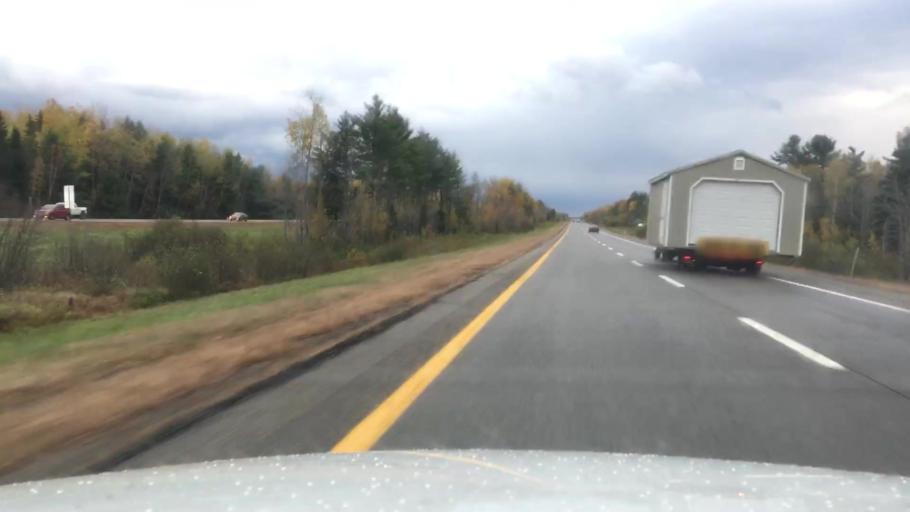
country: US
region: Maine
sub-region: Penobscot County
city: Howland
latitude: 45.2568
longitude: -68.6803
